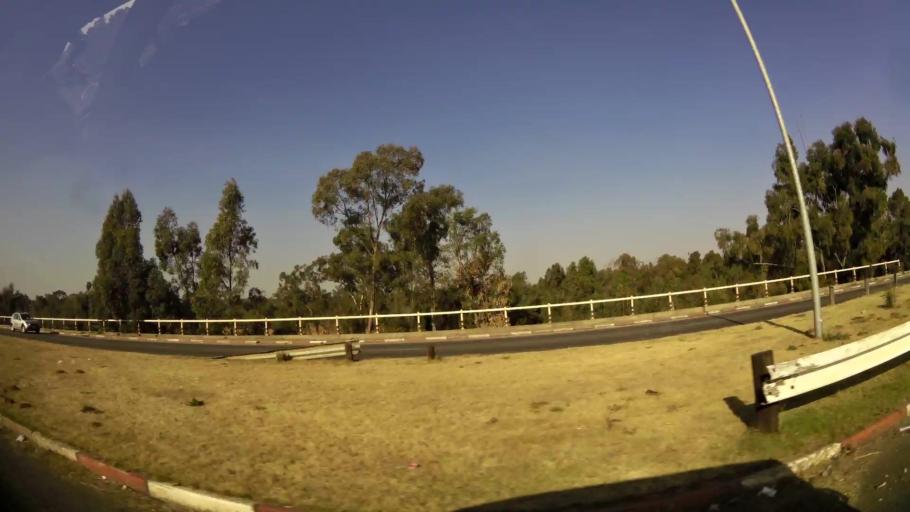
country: ZA
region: Gauteng
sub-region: West Rand District Municipality
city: Randfontein
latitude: -26.1623
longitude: 27.7135
